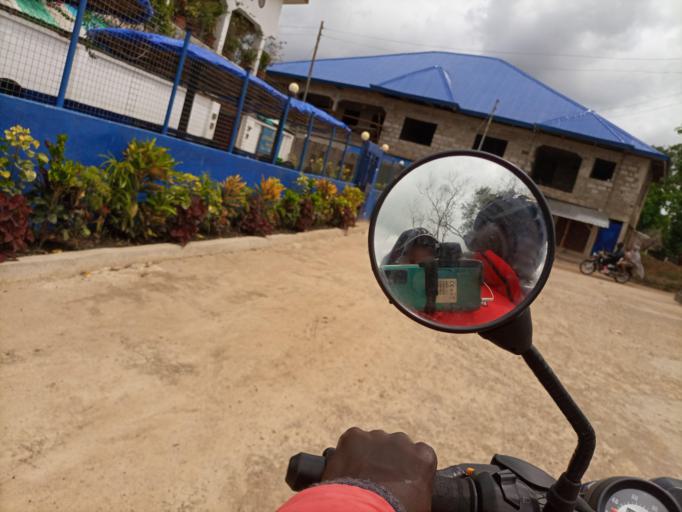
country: SL
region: Southern Province
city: Bo
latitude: 7.9698
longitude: -11.7198
